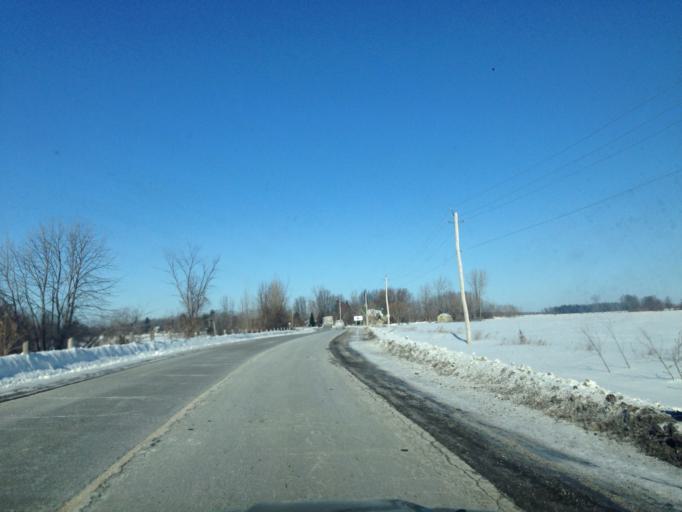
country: CA
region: Ontario
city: Bourget
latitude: 45.2536
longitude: -75.3892
